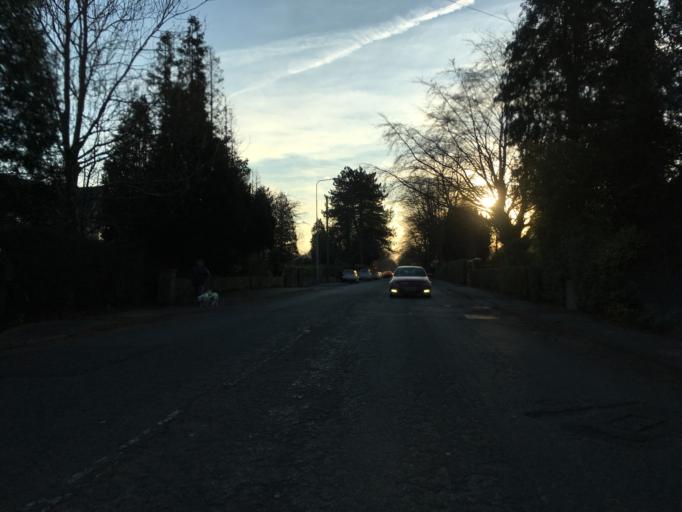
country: GB
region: England
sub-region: Cheshire East
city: Wilmslow
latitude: 53.3407
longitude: -2.2215
